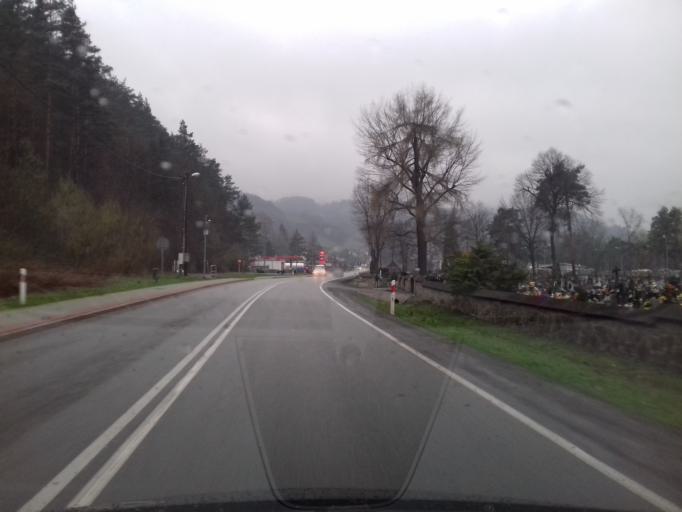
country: PL
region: Lesser Poland Voivodeship
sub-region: Powiat nowosadecki
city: Piwniczna-Zdroj
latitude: 49.4473
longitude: 20.7066
